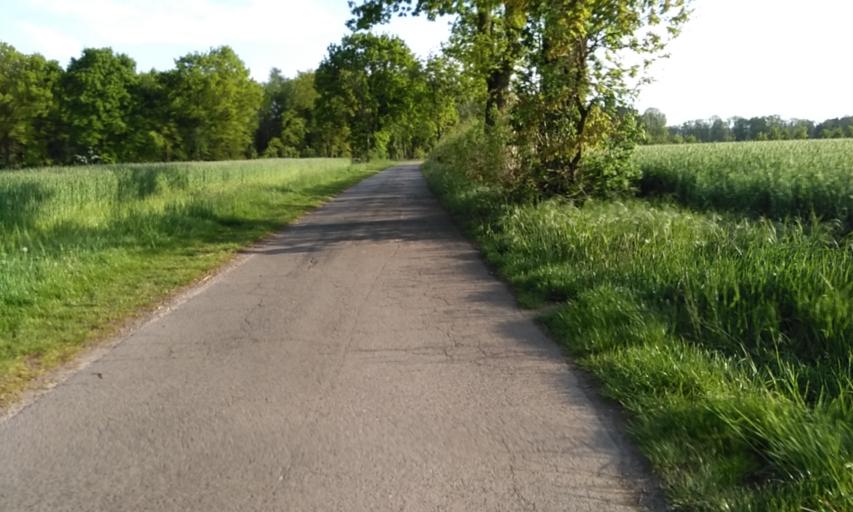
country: DE
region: Lower Saxony
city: Horneburg
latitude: 53.5003
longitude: 9.5634
